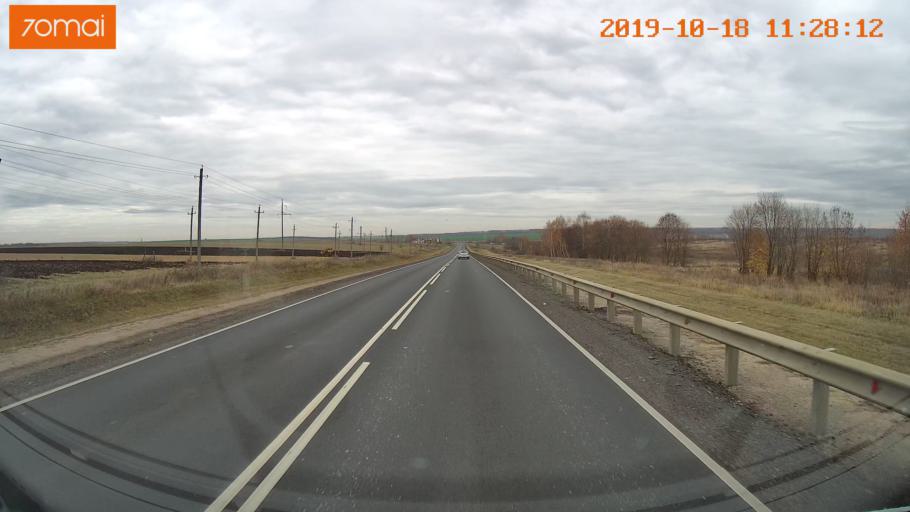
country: RU
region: Tula
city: Kimovsk
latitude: 54.1527
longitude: 38.6567
